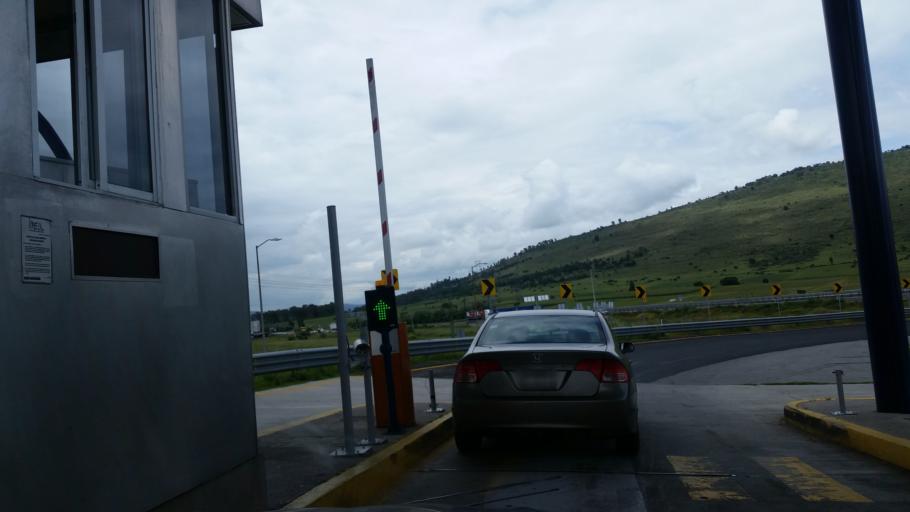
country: MX
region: Mexico
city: San Francisco Soyaniquilpan
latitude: 19.9978
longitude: -99.4918
